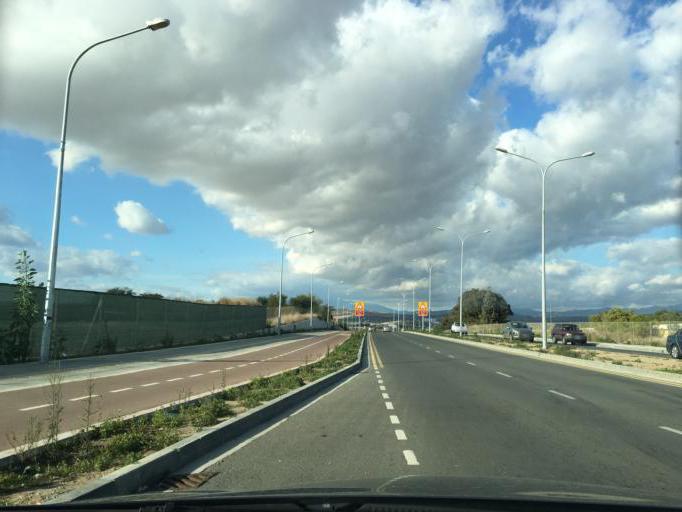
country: CY
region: Limassol
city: Ypsonas
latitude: 34.6681
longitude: 32.9897
